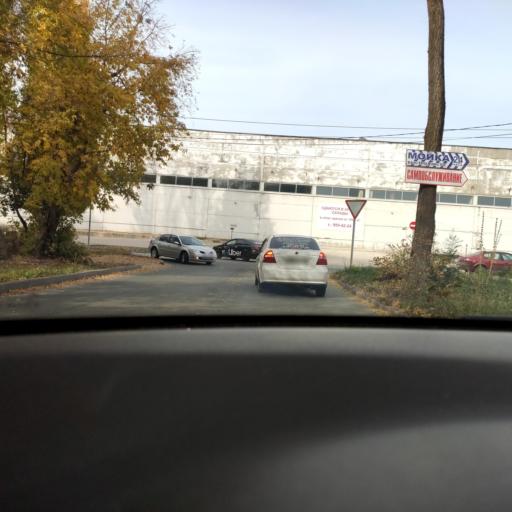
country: RU
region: Samara
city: Samara
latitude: 53.2369
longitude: 50.2442
